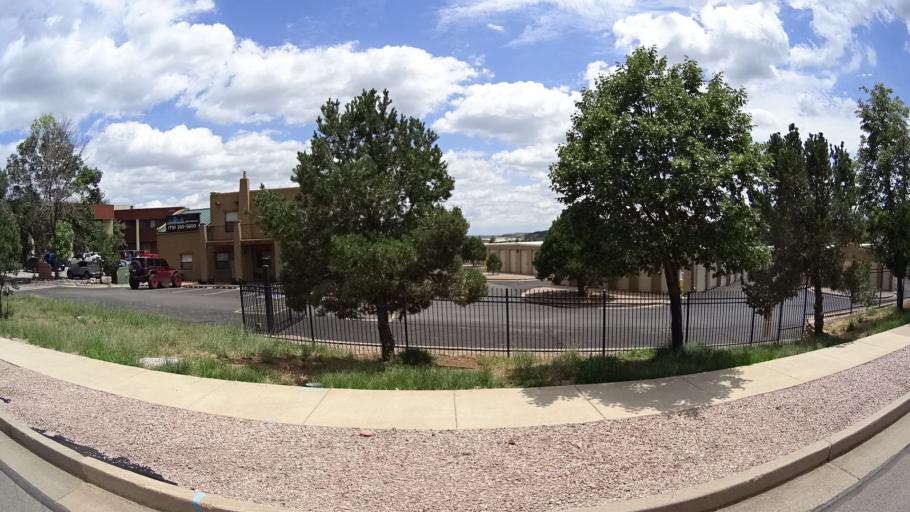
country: US
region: Colorado
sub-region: El Paso County
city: Manitou Springs
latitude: 38.9016
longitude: -104.8680
